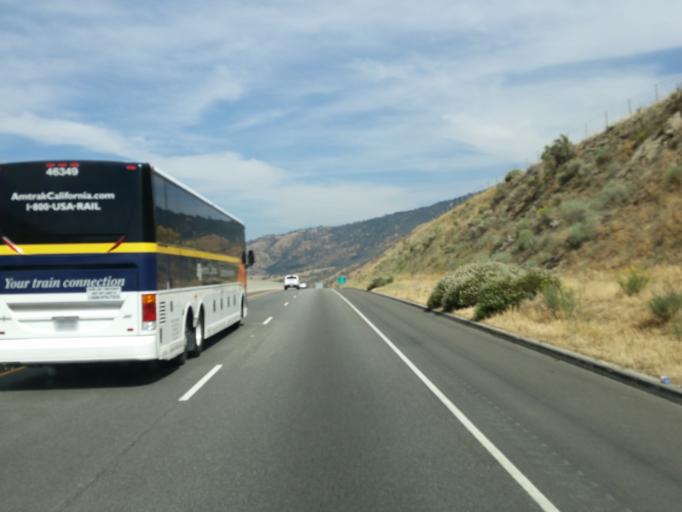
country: US
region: California
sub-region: Kern County
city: Bear Valley Springs
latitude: 35.2688
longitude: -118.6753
